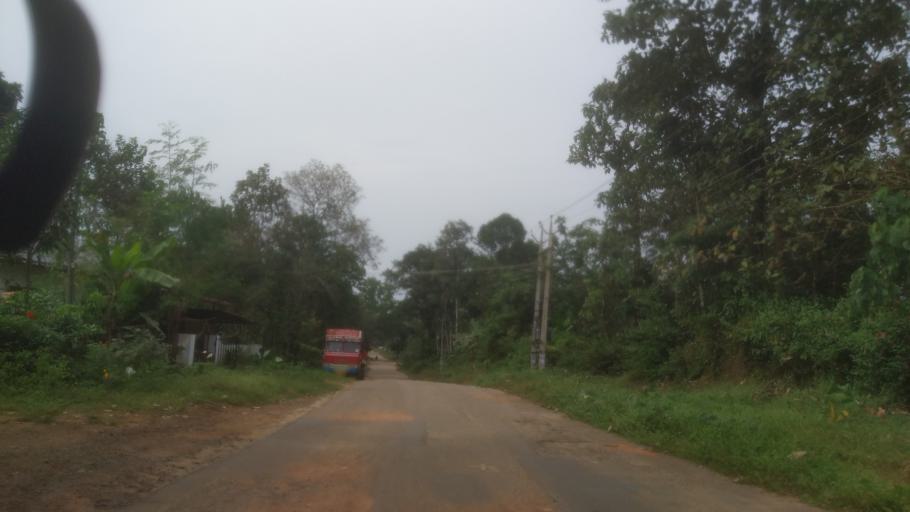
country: IN
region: Kerala
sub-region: Ernakulam
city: Perumbavoor
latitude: 10.0504
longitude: 76.5230
